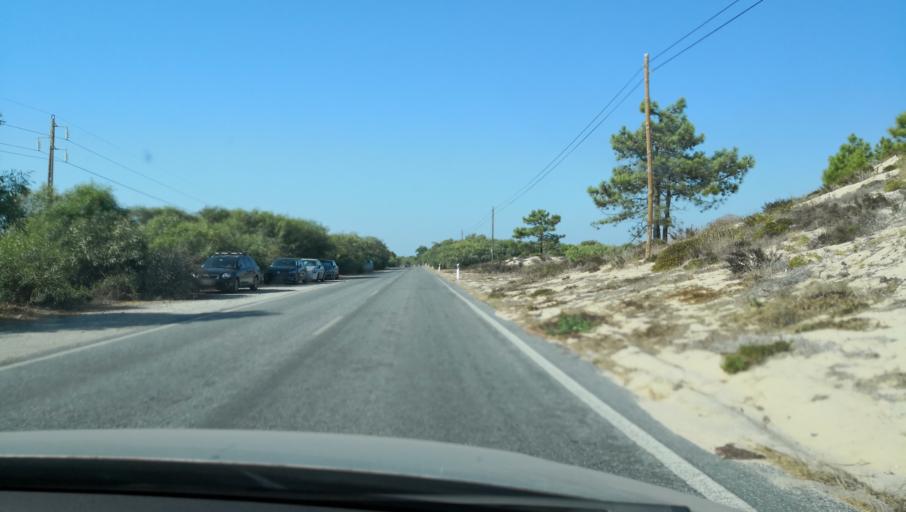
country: PT
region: Setubal
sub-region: Setubal
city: Setubal
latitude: 38.3994
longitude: -8.8060
